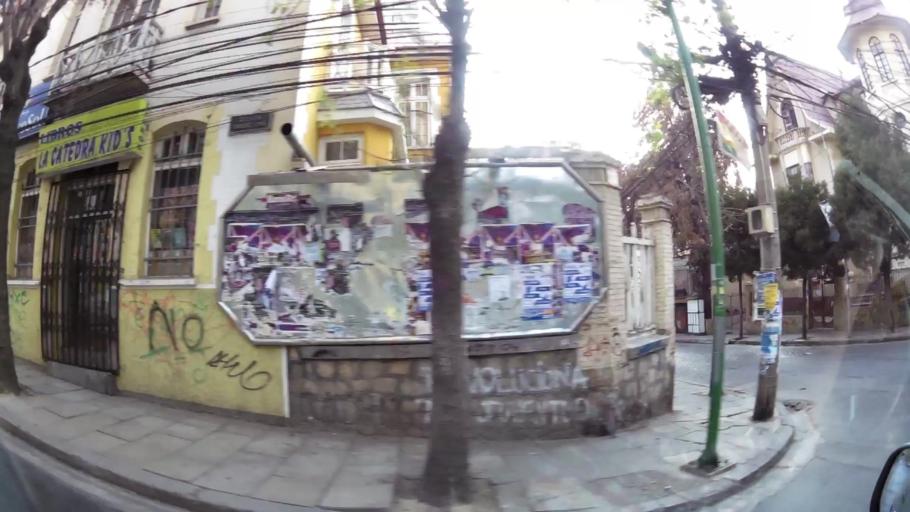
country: BO
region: La Paz
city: La Paz
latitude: -16.5090
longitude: -68.1292
